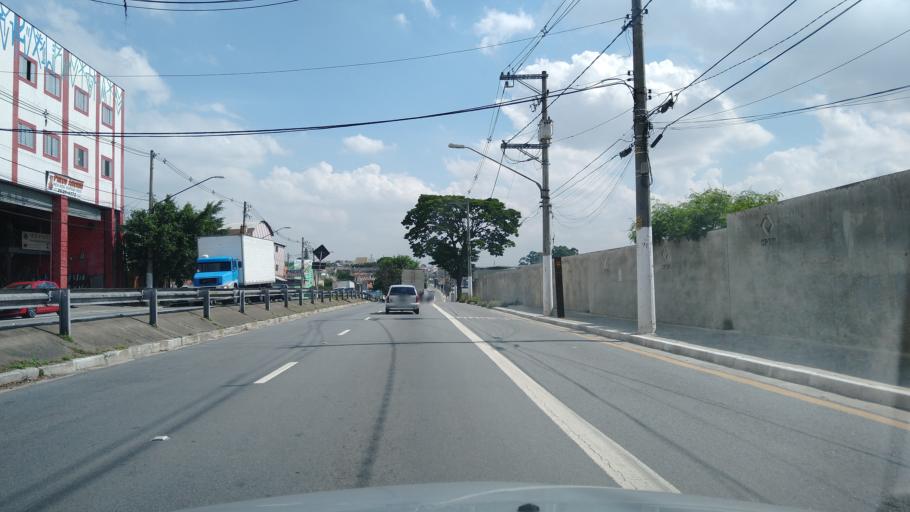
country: BR
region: Sao Paulo
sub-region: Guarulhos
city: Guarulhos
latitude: -23.4967
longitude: -46.5151
